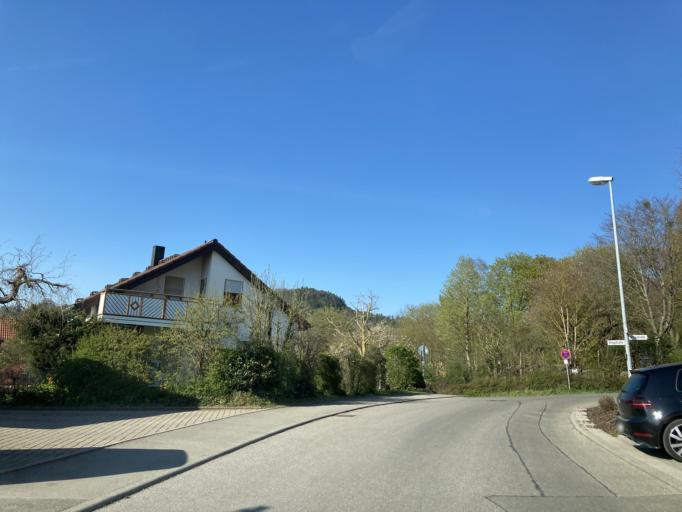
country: DE
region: Baden-Wuerttemberg
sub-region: Regierungsbezirk Stuttgart
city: Hildrizhausen
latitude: 48.5534
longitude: 8.9738
